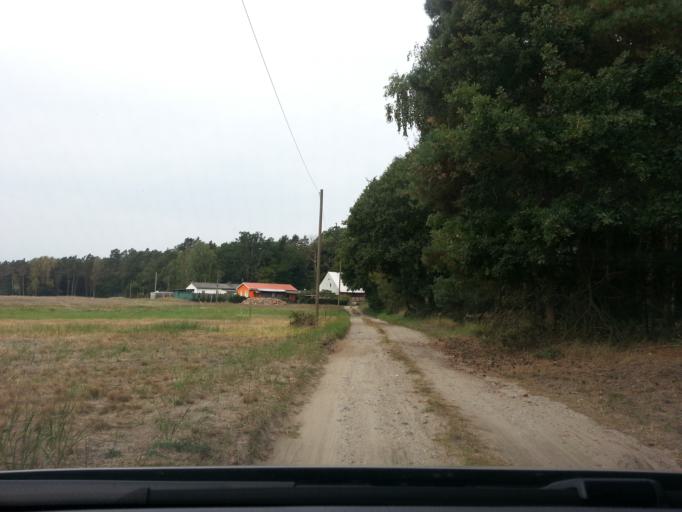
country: DE
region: Mecklenburg-Vorpommern
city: Ferdinandshof
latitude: 53.7105
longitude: 13.9330
